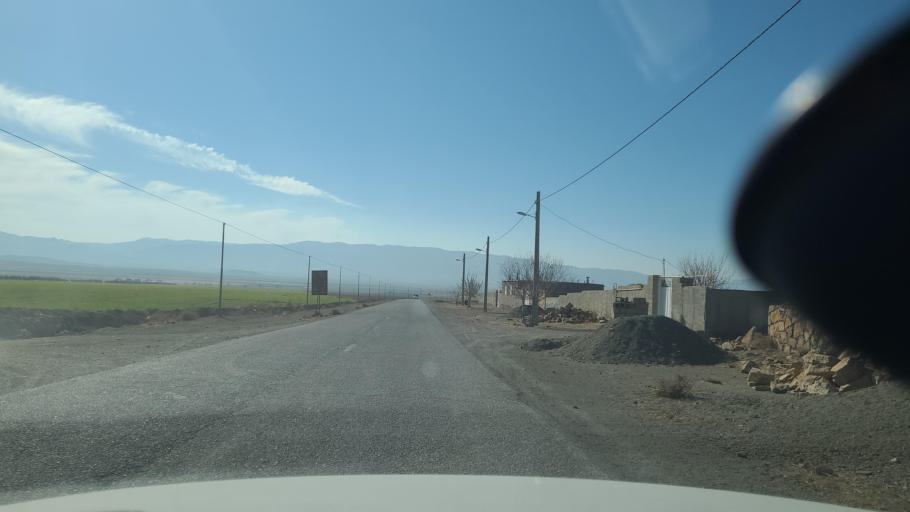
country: IR
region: Razavi Khorasan
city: Dowlatabad
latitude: 35.6169
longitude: 59.4750
